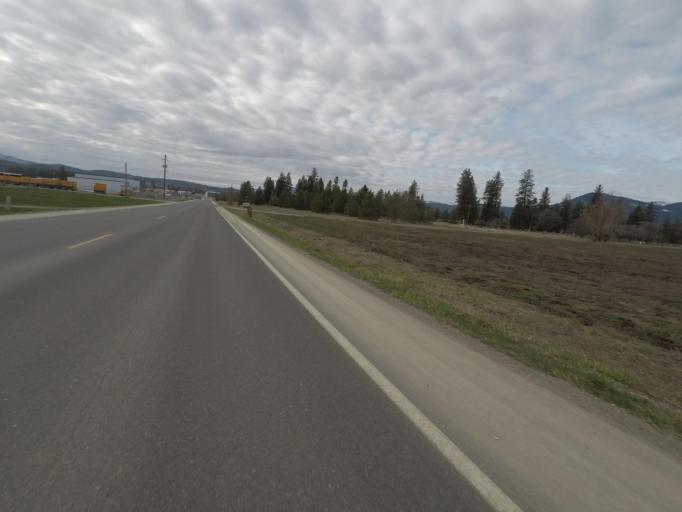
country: US
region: Washington
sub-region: Stevens County
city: Colville
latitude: 48.5518
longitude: -117.8821
